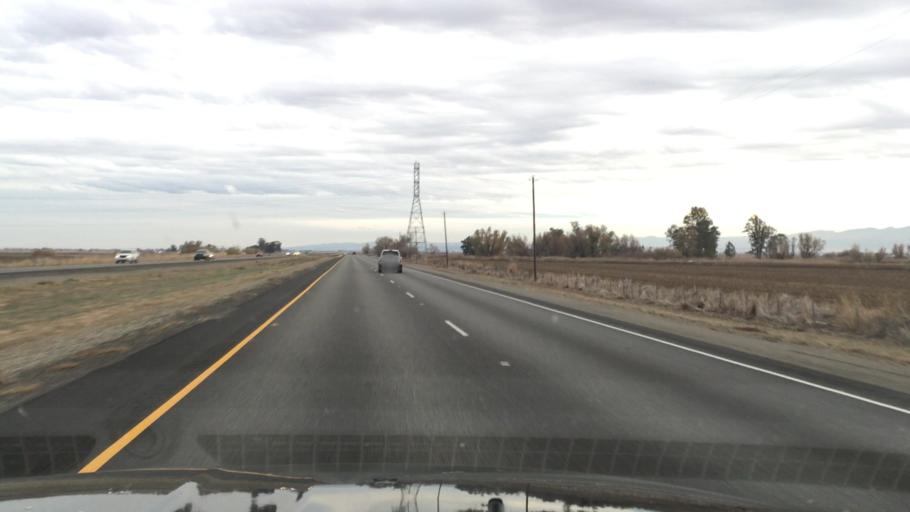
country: US
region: California
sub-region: Colusa County
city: Maxwell
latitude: 39.2166
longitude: -122.1812
